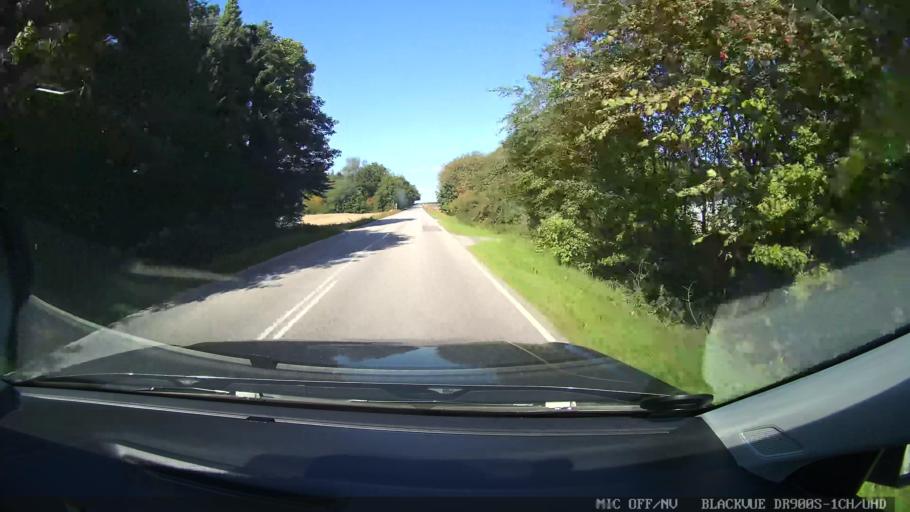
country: DK
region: North Denmark
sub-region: Mariagerfjord Kommune
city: Mariager
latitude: 56.6300
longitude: 9.9803
